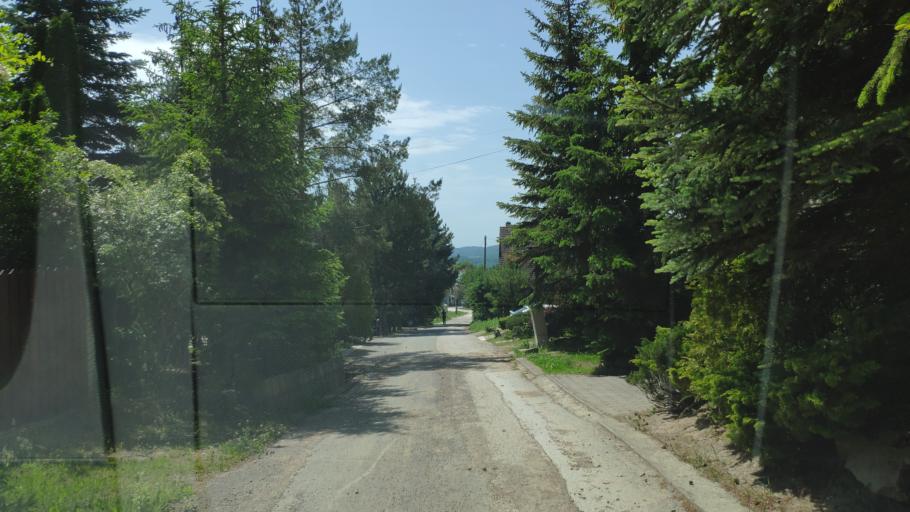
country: SK
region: Kosicky
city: Medzev
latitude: 48.7170
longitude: 20.9807
